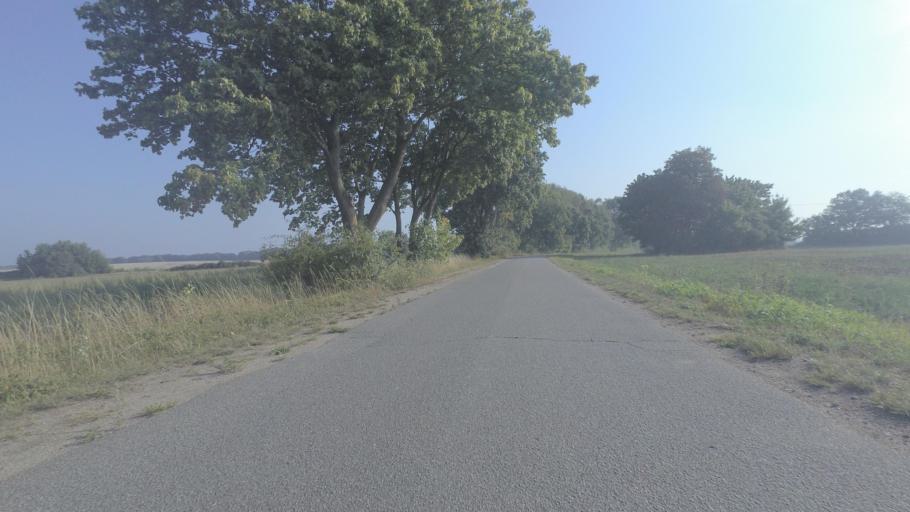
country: DE
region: Mecklenburg-Vorpommern
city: Malchow
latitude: 53.3552
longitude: 12.3654
